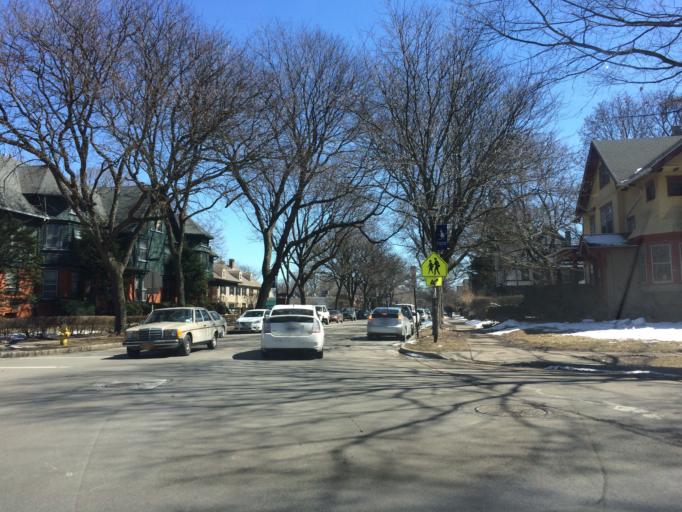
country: US
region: New York
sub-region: Monroe County
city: Brighton
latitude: 43.1491
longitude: -77.5815
